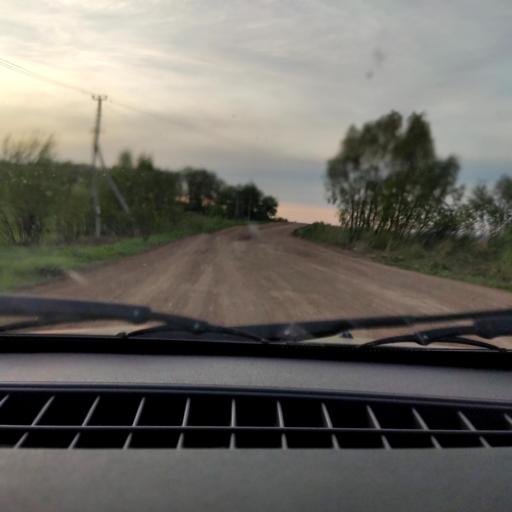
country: RU
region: Bashkortostan
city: Iglino
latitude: 54.8557
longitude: 56.3964
